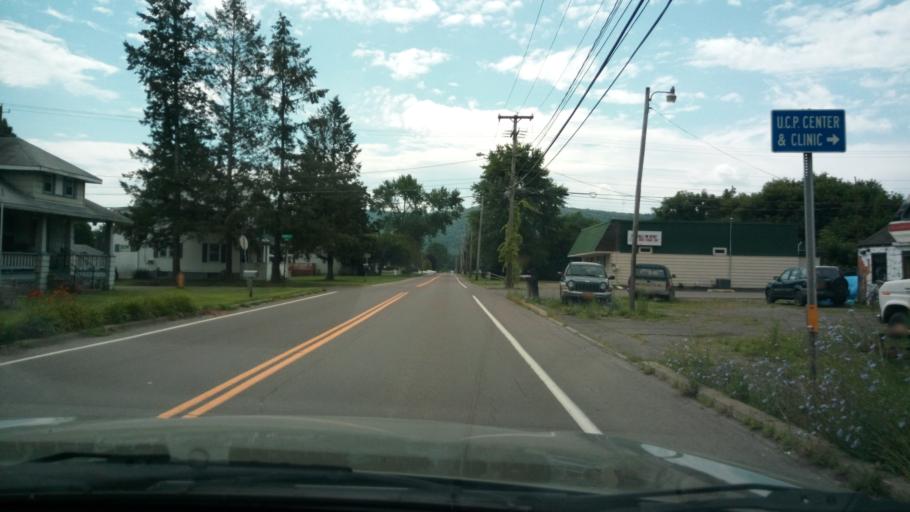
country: US
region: New York
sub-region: Chemung County
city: Southport
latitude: 42.0634
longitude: -76.7952
